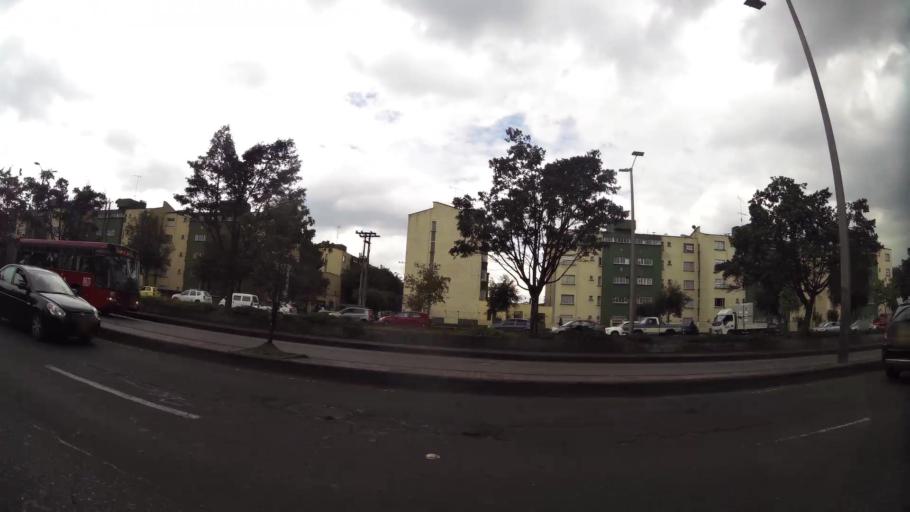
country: CO
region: Bogota D.C.
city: Barrio San Luis
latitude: 4.6793
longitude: -74.0751
